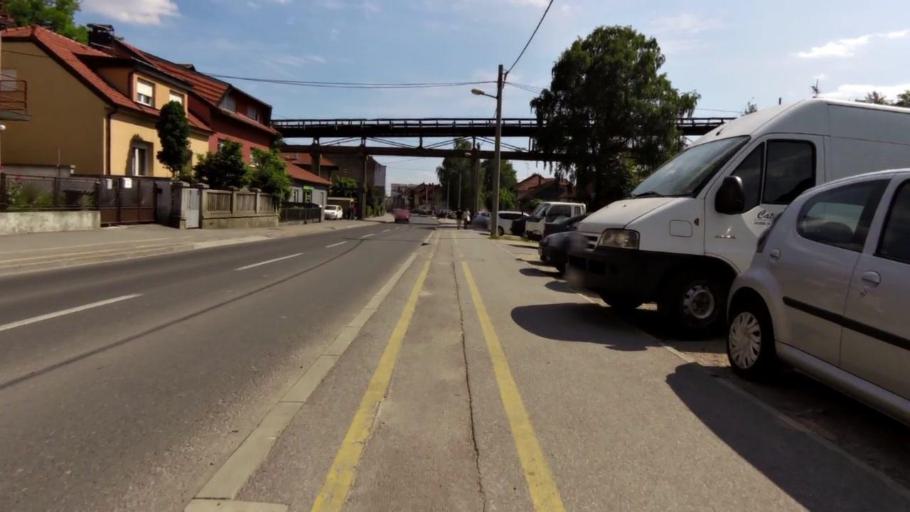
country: HR
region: Grad Zagreb
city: Jankomir
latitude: 45.8167
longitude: 15.9266
